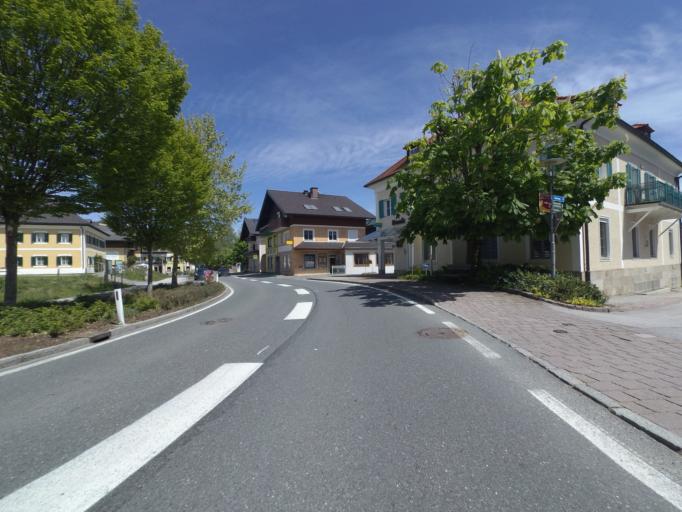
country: AT
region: Salzburg
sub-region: Politischer Bezirk Salzburg-Umgebung
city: Seeham
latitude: 47.9677
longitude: 13.0783
